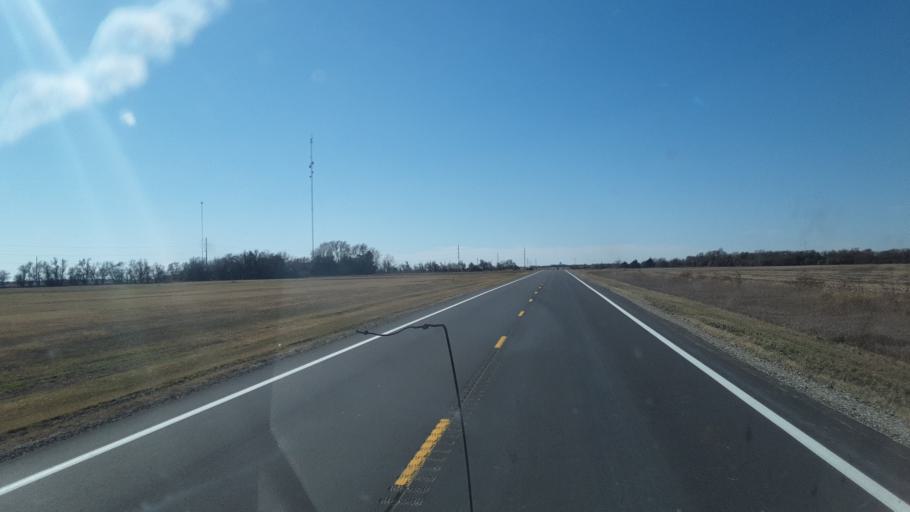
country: US
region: Kansas
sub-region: Rice County
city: Lyons
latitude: 38.3717
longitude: -98.1391
